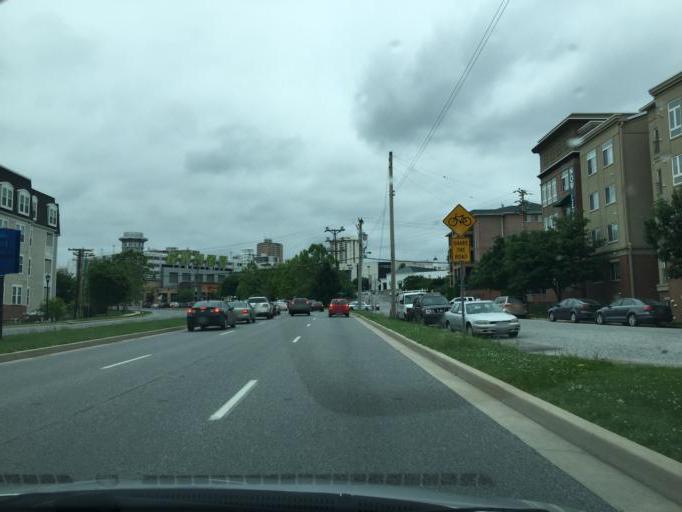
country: US
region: Maryland
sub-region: Baltimore County
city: Towson
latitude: 39.4073
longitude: -76.6033
